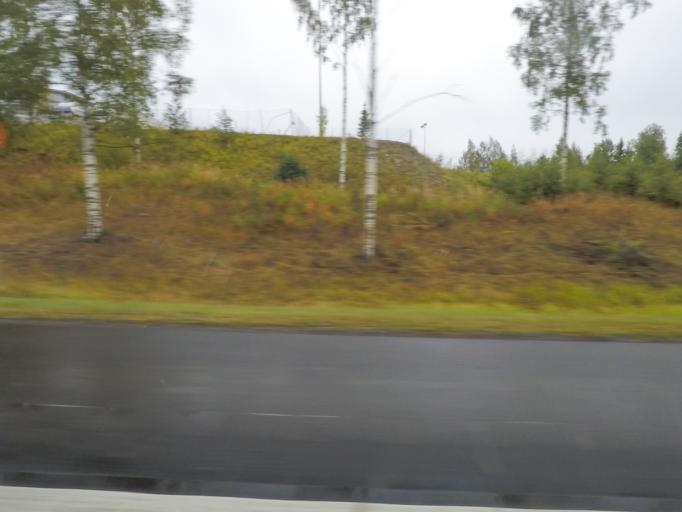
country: FI
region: Northern Savo
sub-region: Kuopio
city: Kuopio
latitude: 62.8678
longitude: 27.6190
